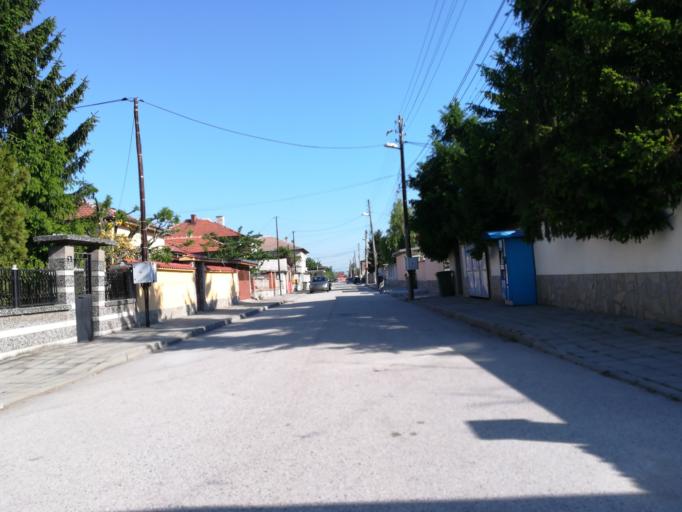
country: BG
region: Stara Zagora
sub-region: Obshtina Chirpan
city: Chirpan
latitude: 42.1023
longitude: 25.2329
